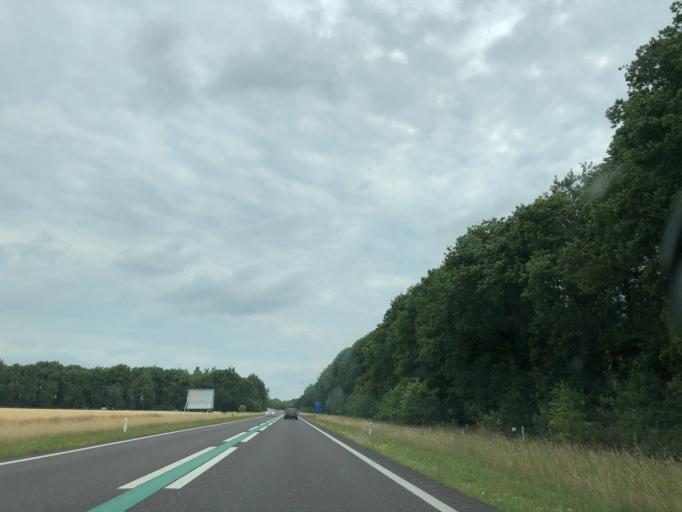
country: NL
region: Drenthe
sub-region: Gemeente Aa en Hunze
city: Anloo
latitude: 53.0556
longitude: 6.7079
